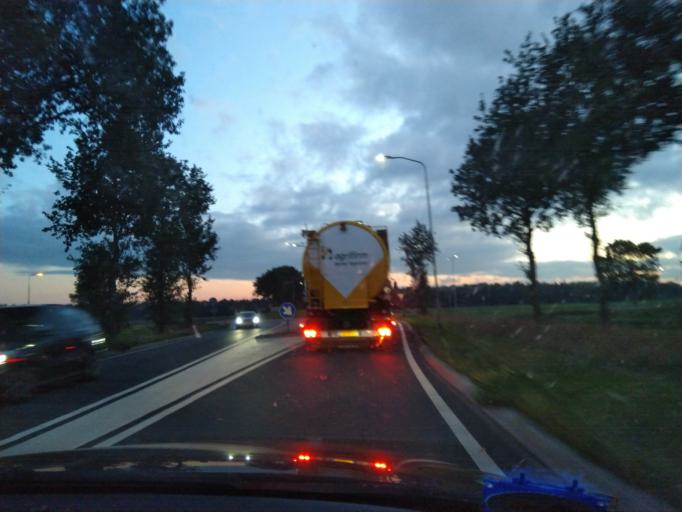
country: NL
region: Groningen
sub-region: Gemeente Pekela
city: Oude Pekela
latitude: 53.0895
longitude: 6.9714
